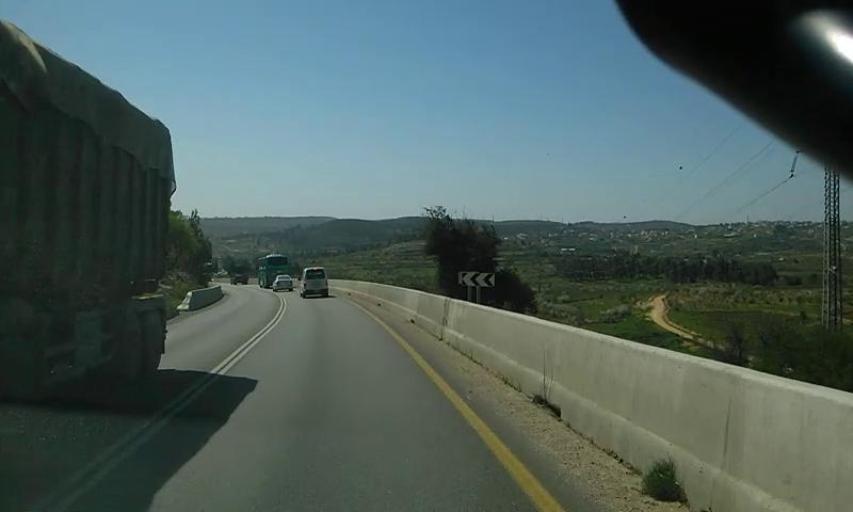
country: PS
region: West Bank
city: Shuyukh al `Arrub
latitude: 31.6404
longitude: 35.1315
